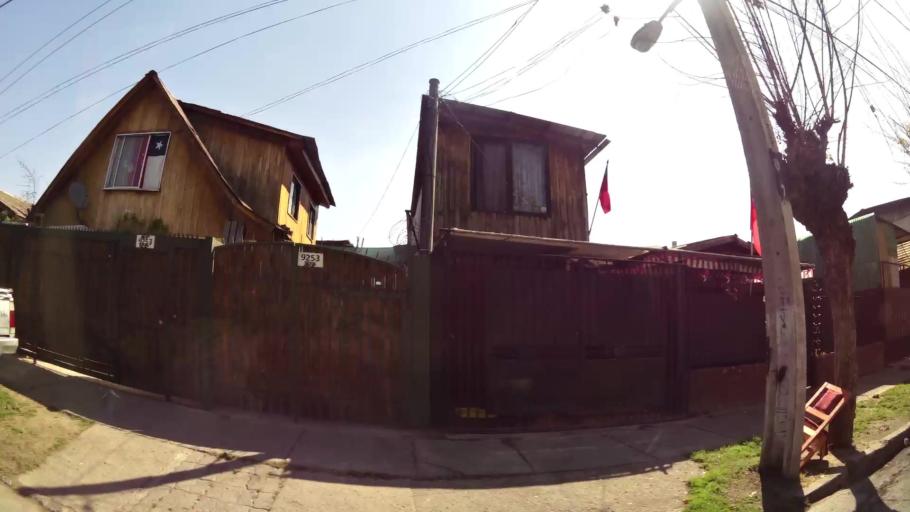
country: CL
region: Santiago Metropolitan
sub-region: Provincia de Santiago
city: La Pintana
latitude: -33.5388
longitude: -70.6070
